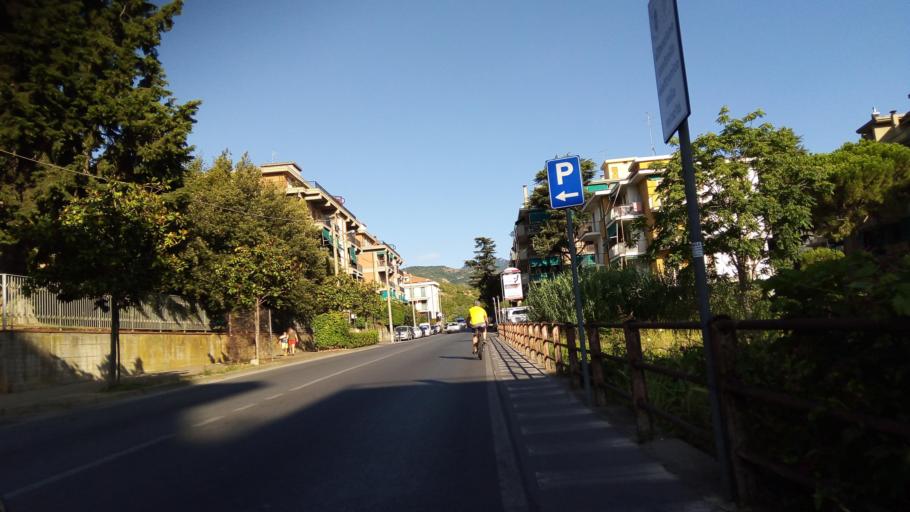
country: IT
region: Liguria
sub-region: Provincia di Savona
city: Borghetto Santo Spirito
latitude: 44.1128
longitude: 8.2348
